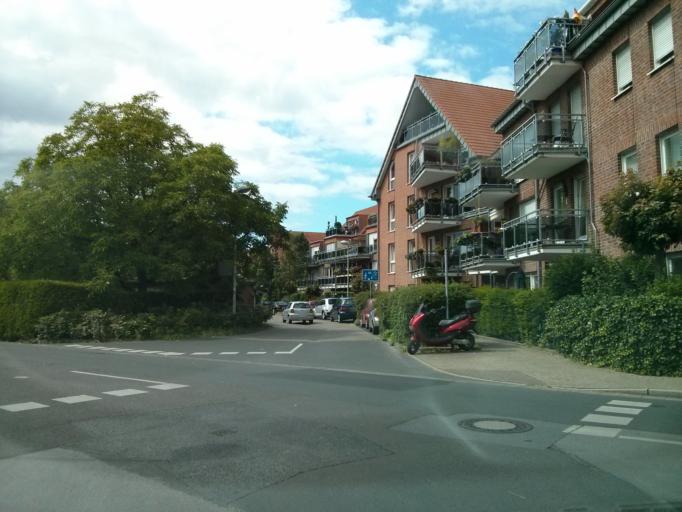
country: DE
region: North Rhine-Westphalia
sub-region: Regierungsbezirk Dusseldorf
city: Krefeld
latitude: 51.3072
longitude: 6.5803
